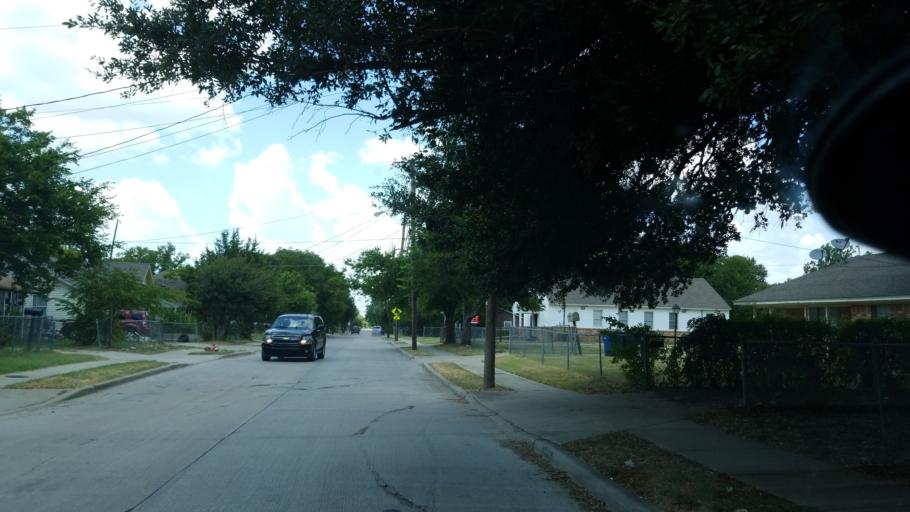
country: US
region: Texas
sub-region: Dallas County
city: Cockrell Hill
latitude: 32.7504
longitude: -96.9128
